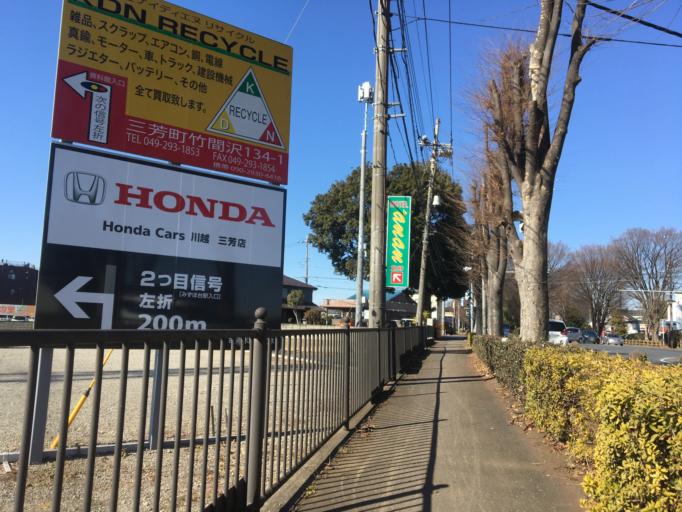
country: JP
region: Saitama
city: Oi
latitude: 35.8209
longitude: 139.5401
